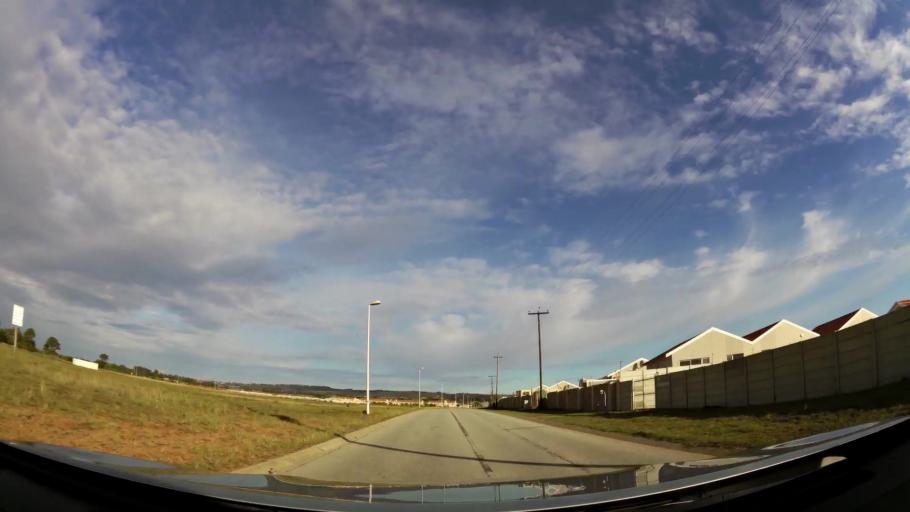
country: ZA
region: Eastern Cape
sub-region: Nelson Mandela Bay Metropolitan Municipality
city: Port Elizabeth
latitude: -33.9496
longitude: 25.4870
